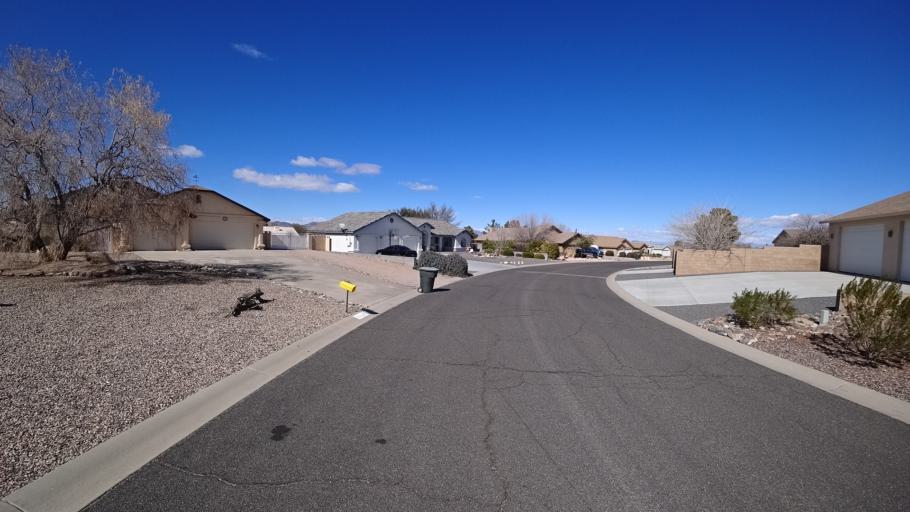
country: US
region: Arizona
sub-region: Mohave County
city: Kingman
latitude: 35.1983
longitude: -113.9683
